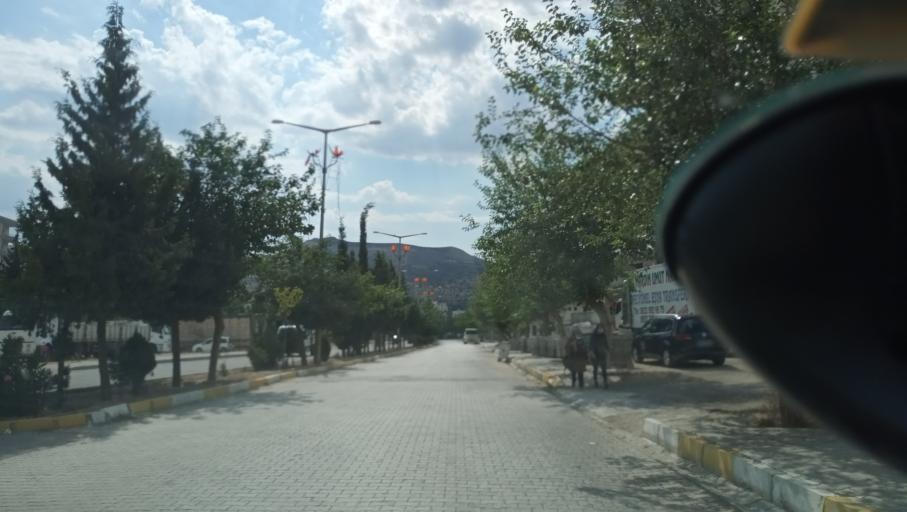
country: TR
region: Mardin
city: Kabala
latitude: 37.3401
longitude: 40.8140
